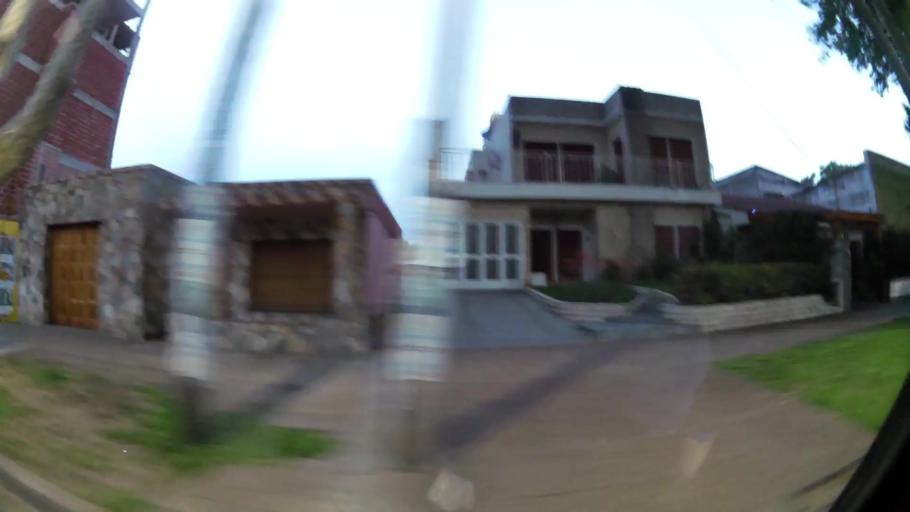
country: AR
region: Buenos Aires
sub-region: Partido de Quilmes
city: Quilmes
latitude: -34.8033
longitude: -58.2802
